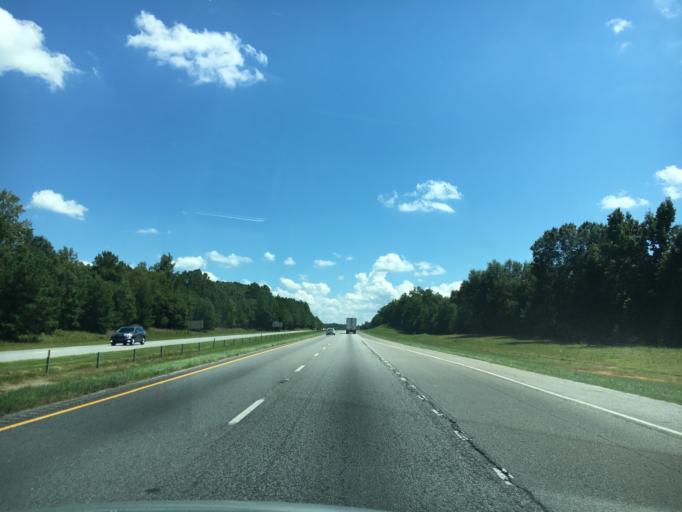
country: US
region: South Carolina
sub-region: Spartanburg County
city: Roebuck
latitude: 34.8340
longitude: -81.9692
